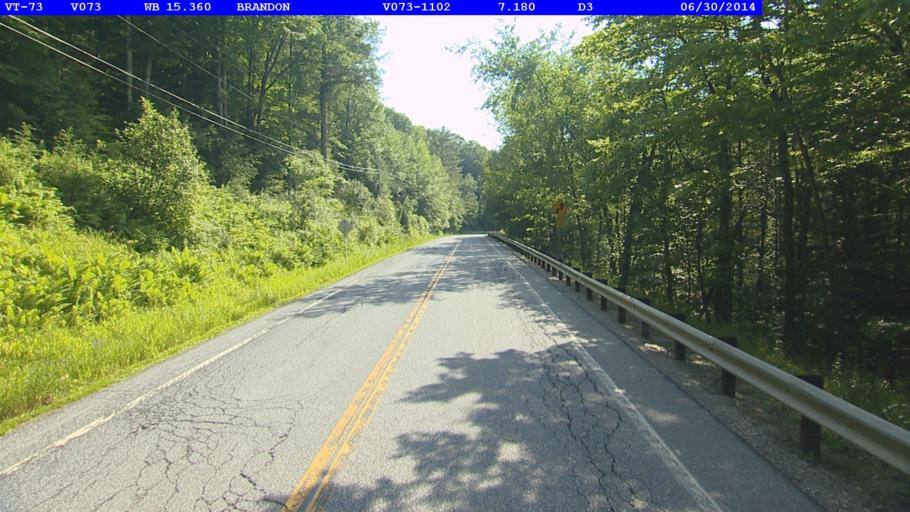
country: US
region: Vermont
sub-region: Rutland County
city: Brandon
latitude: 43.8391
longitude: -73.0352
